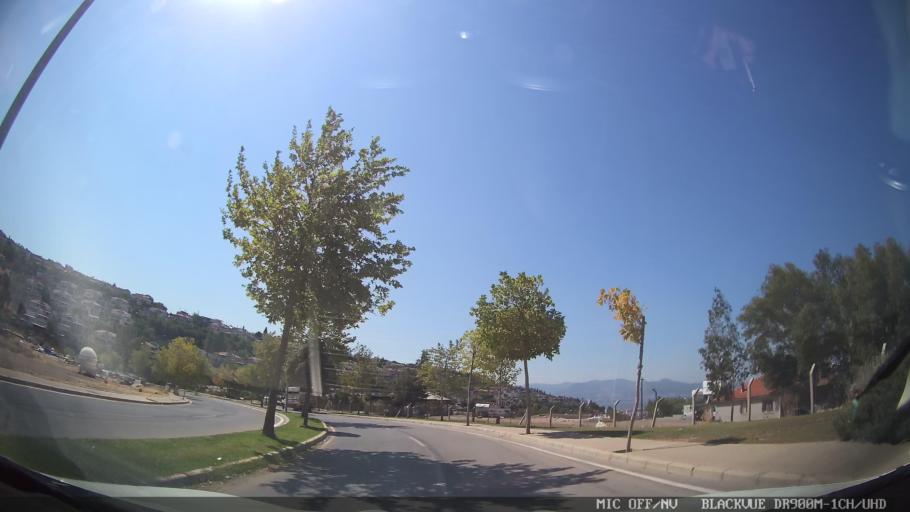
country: TR
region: Izmir
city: Karsiyaka
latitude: 38.5041
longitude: 27.0826
